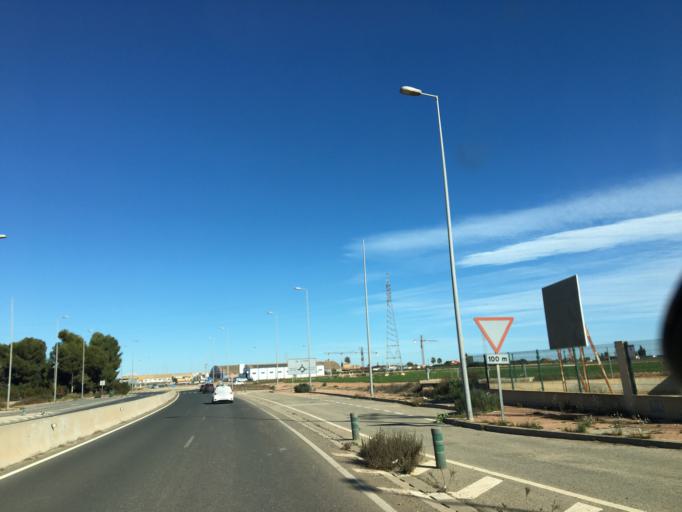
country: ES
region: Murcia
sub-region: Murcia
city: Cartagena
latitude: 37.6420
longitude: -0.9865
